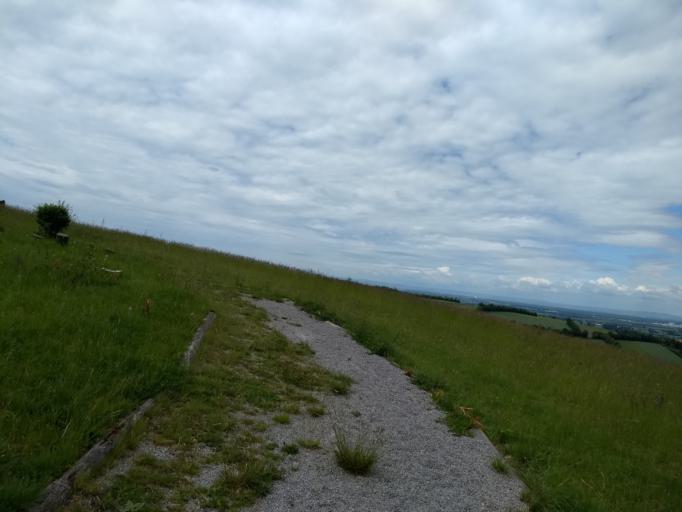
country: AT
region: Lower Austria
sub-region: Politischer Bezirk Tulln
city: Tulbing
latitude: 48.2716
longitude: 16.1041
